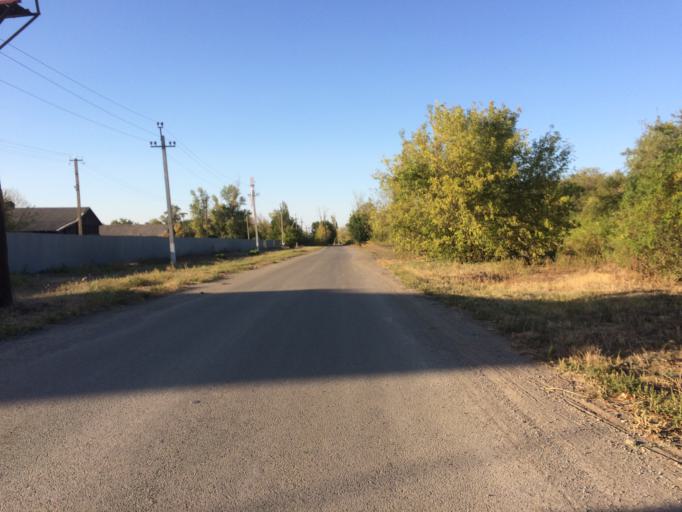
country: RU
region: Rostov
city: Gigant
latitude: 46.5139
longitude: 41.1922
